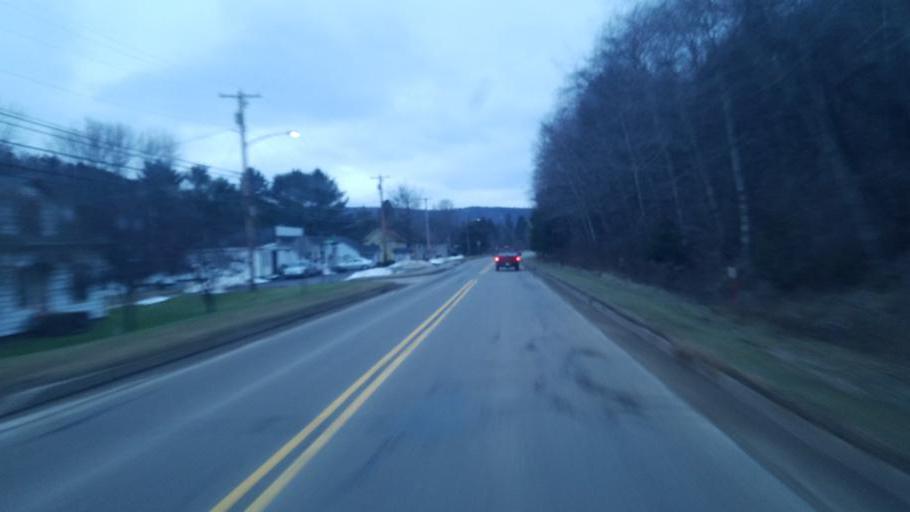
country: US
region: Pennsylvania
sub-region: Potter County
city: Coudersport
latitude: 41.7844
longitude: -78.0176
